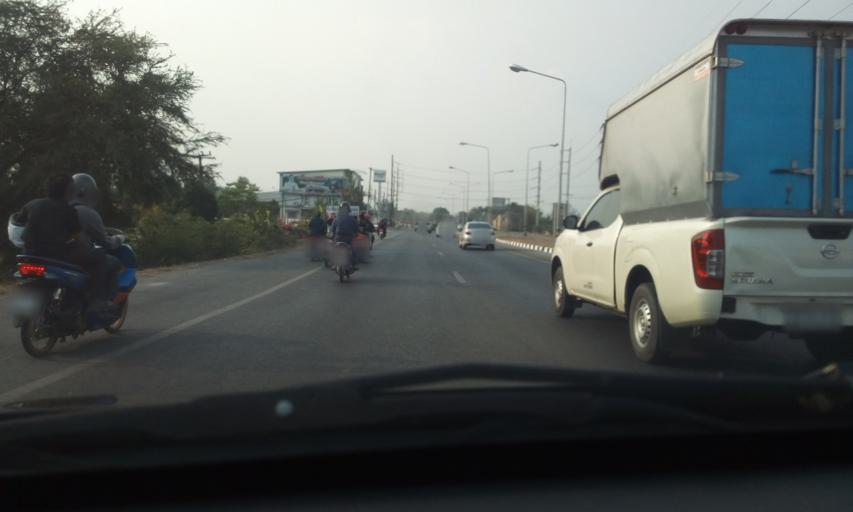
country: TH
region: Nakhon Nayok
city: Nakhon Nayok
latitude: 14.2027
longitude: 101.1899
